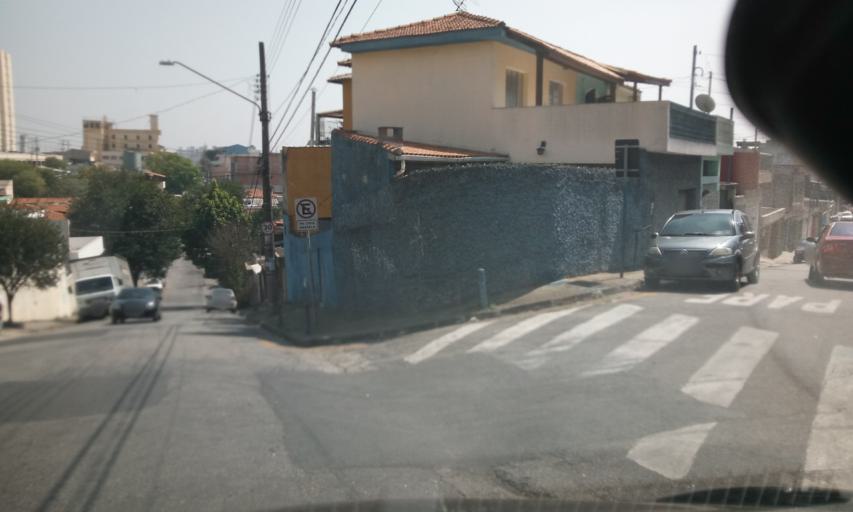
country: BR
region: Sao Paulo
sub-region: Sao Bernardo Do Campo
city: Sao Bernardo do Campo
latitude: -23.6976
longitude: -46.5677
